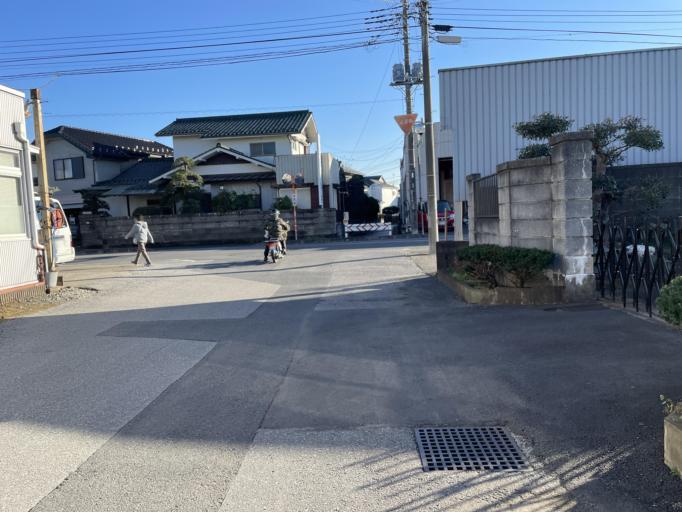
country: JP
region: Saitama
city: Kurihashi
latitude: 36.1369
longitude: 139.6999
